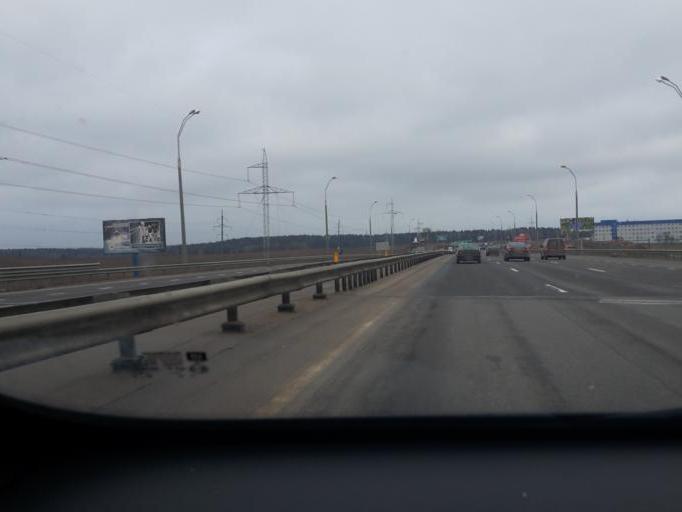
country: BY
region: Minsk
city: Novoye Medvezhino
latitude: 53.8952
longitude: 27.4103
